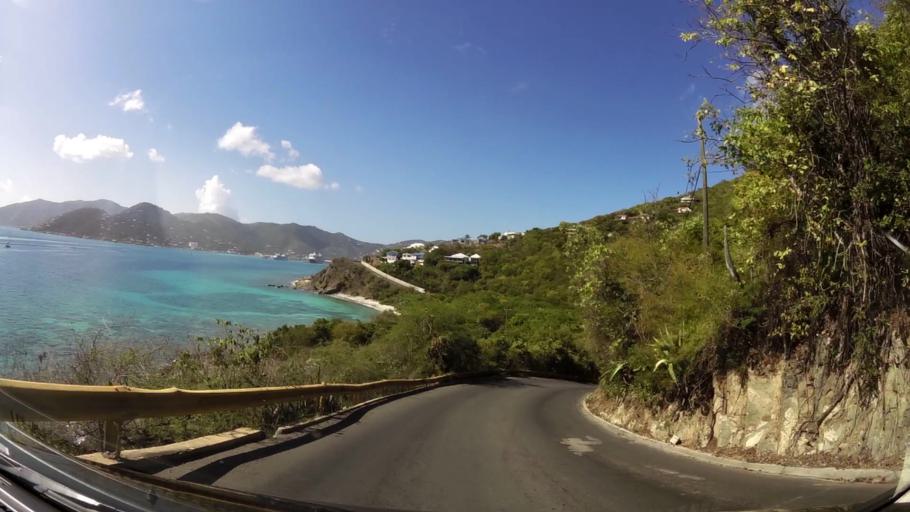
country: VG
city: Tortola
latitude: 18.4123
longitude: -64.5913
